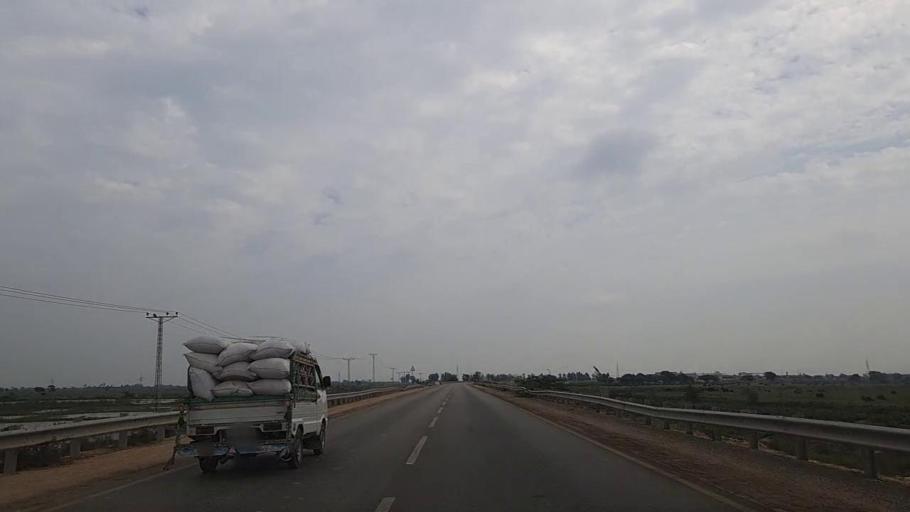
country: PK
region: Sindh
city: Daro Mehar
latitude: 24.6183
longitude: 68.0807
